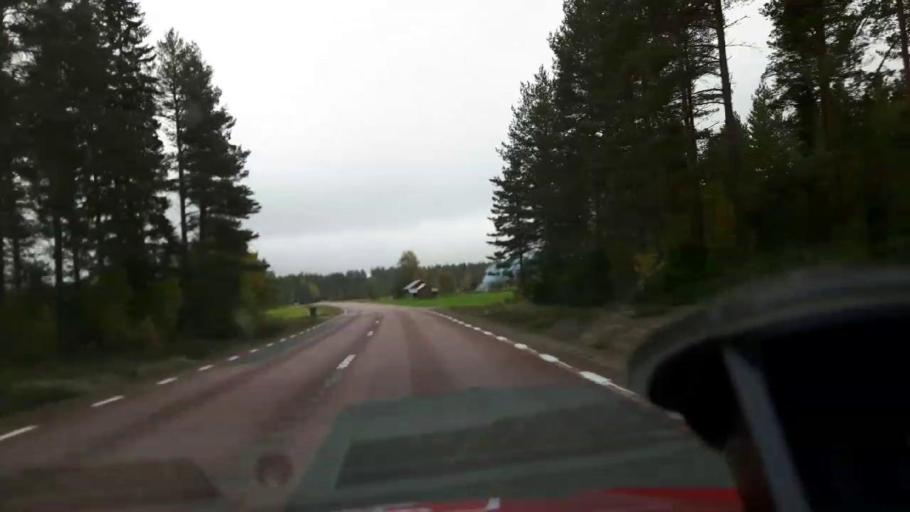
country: SE
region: Gaevleborg
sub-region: Ljusdals Kommun
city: Farila
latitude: 61.8427
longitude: 15.7506
